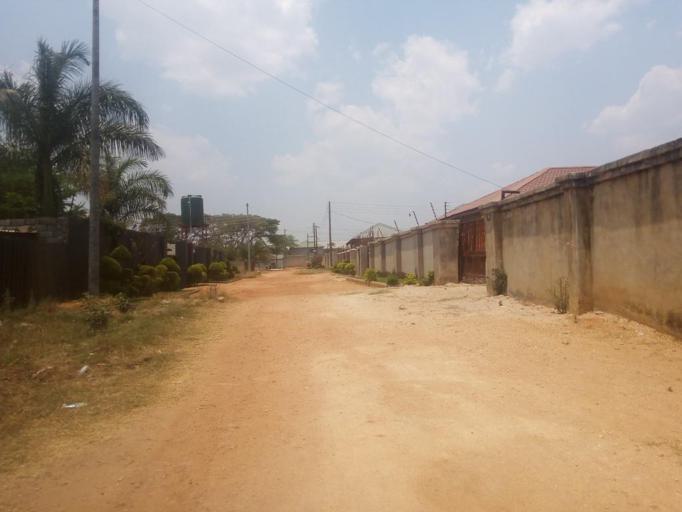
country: ZM
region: Lusaka
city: Lusaka
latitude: -15.3951
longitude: 28.3921
